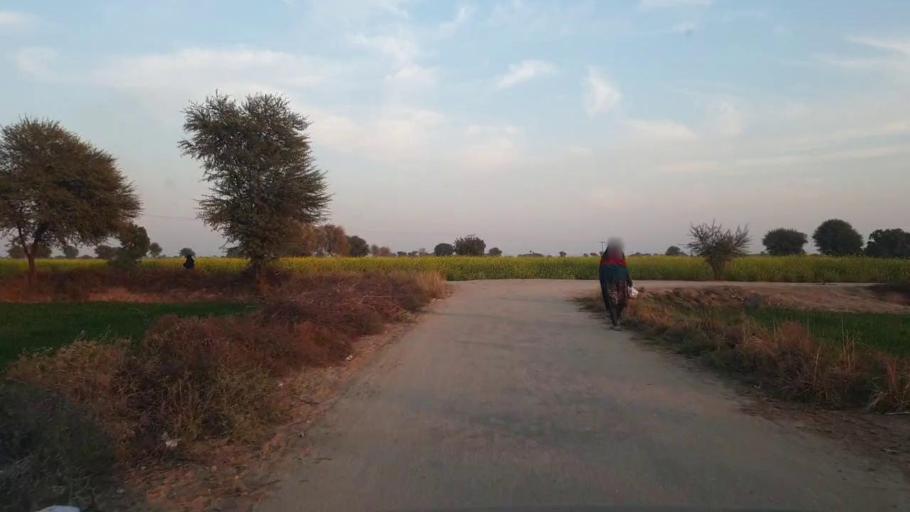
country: PK
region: Sindh
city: Shahpur Chakar
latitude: 26.1776
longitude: 68.6153
